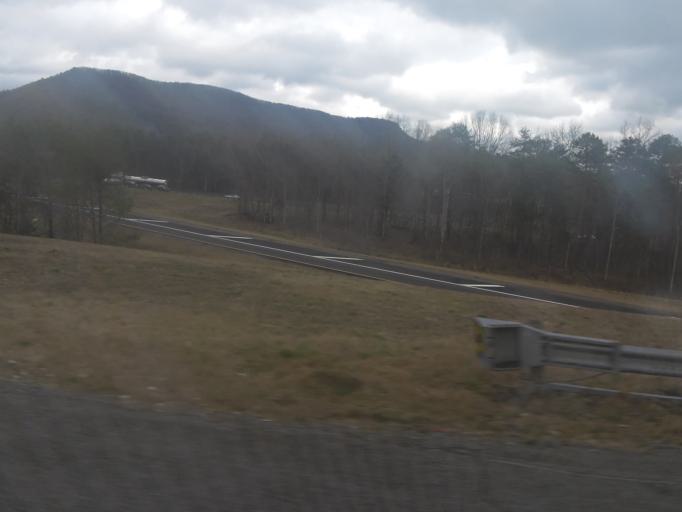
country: US
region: Georgia
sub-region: Walker County
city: Lookout Mountain
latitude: 34.9722
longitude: -85.4528
